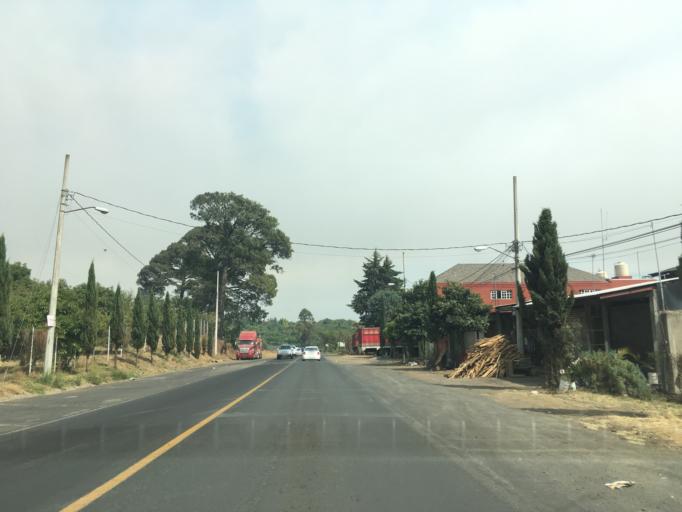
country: MX
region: Michoacan
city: Nuevo San Juan Parangaricutiro
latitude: 19.4066
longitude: -102.1138
